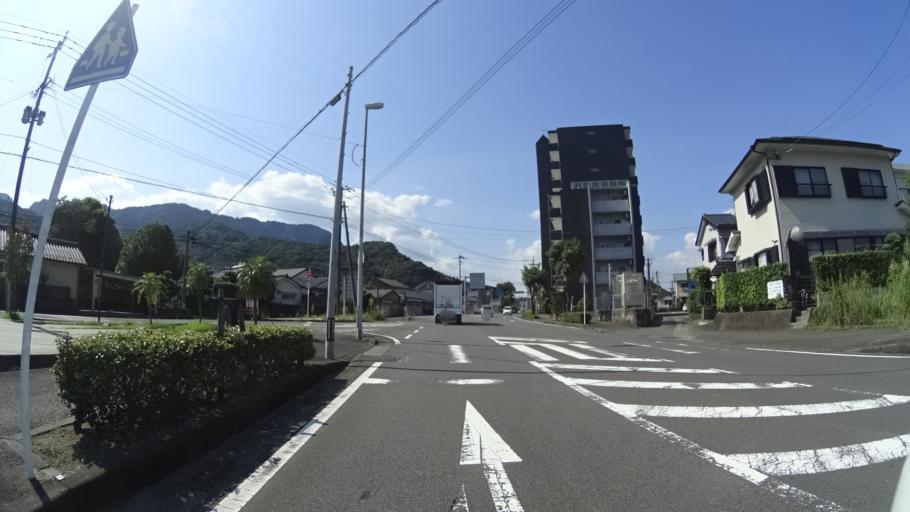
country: JP
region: Kagoshima
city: Kajiki
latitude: 31.7107
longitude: 130.6024
